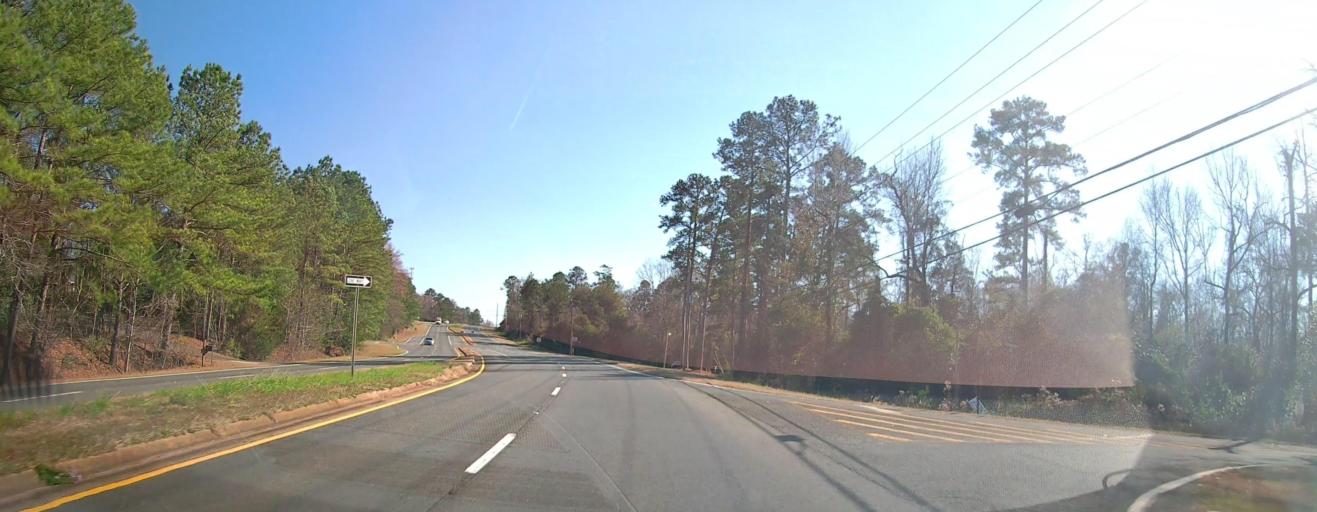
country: US
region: Georgia
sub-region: Sumter County
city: Americus
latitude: 32.1011
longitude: -84.2443
